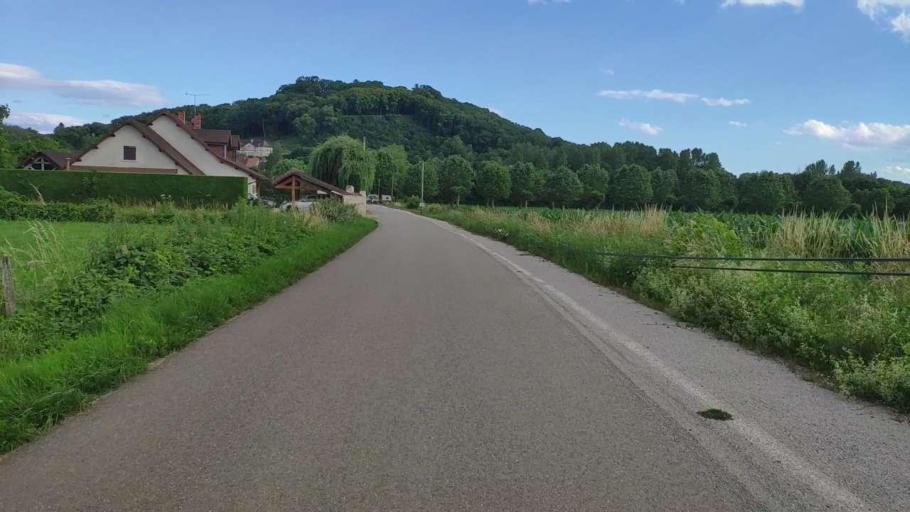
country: FR
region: Franche-Comte
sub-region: Departement du Jura
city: Bletterans
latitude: 46.7644
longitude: 5.5349
